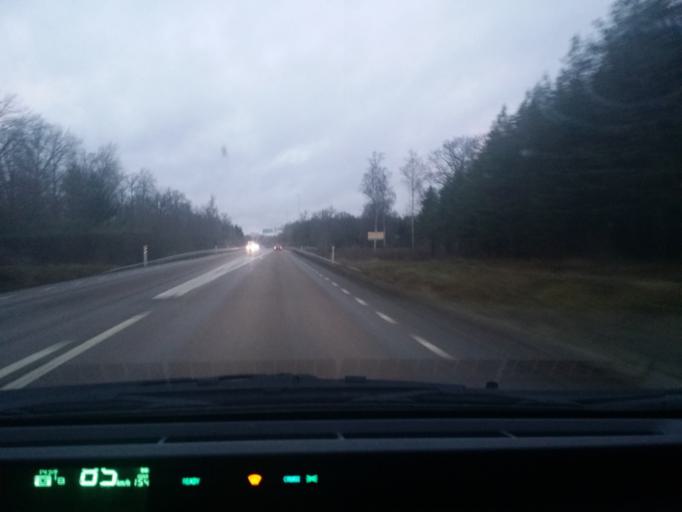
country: SE
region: Soedermanland
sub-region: Eskilstuna Kommun
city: Kvicksund
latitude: 59.4927
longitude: 16.3052
